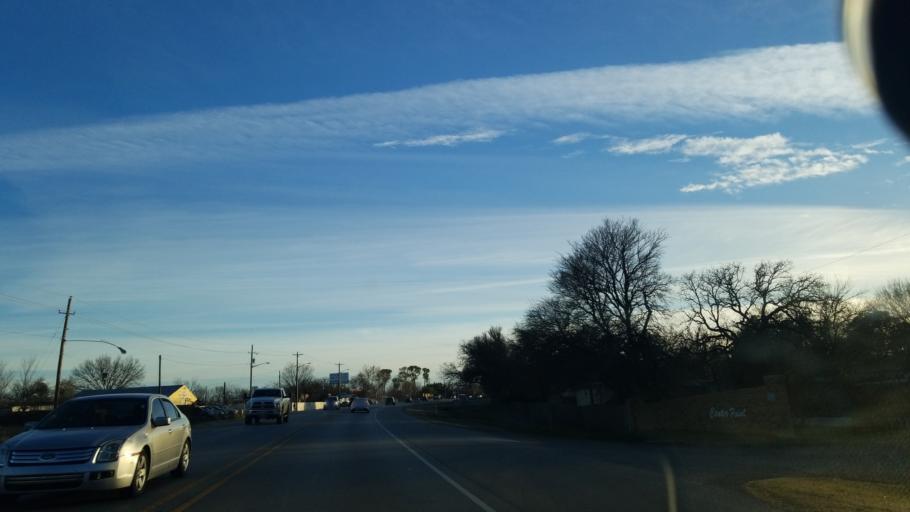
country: US
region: Texas
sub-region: Denton County
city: Denton
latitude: 33.1840
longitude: -97.1389
